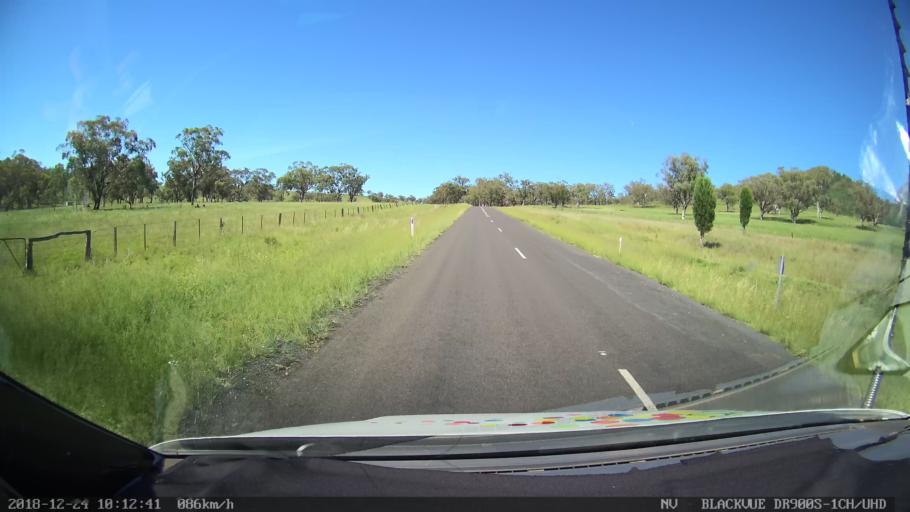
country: AU
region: New South Wales
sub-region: Liverpool Plains
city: Quirindi
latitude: -31.6817
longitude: 150.6455
